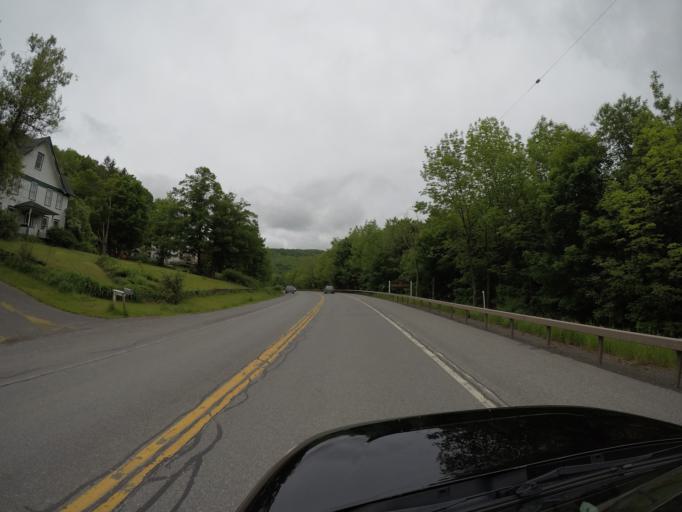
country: US
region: New York
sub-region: Delaware County
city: Stamford
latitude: 42.1477
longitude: -74.6428
